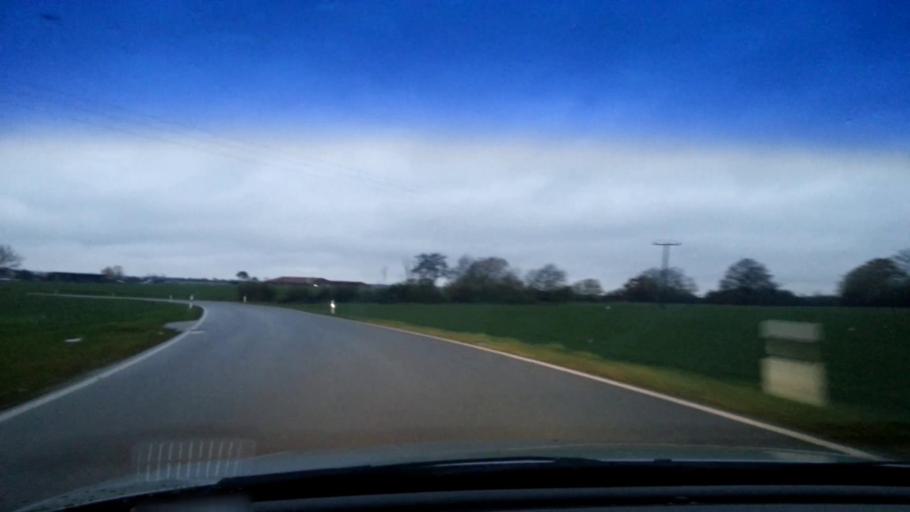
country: DE
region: Bavaria
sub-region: Upper Franconia
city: Schesslitz
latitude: 49.9553
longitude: 11.0255
